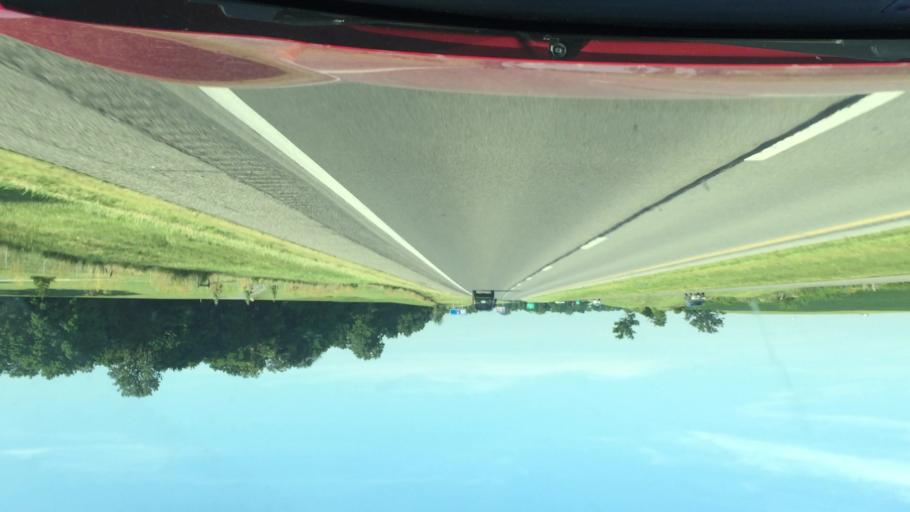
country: US
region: Ohio
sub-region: Logan County
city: Bellefontaine
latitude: 40.3938
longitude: -83.7783
